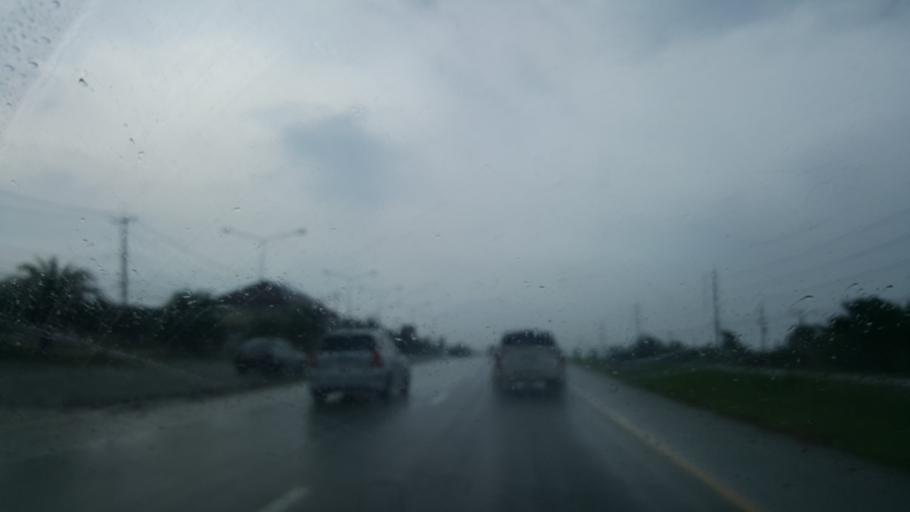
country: TH
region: Chon Buri
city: Ban Talat Bueng
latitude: 12.9468
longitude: 101.0445
